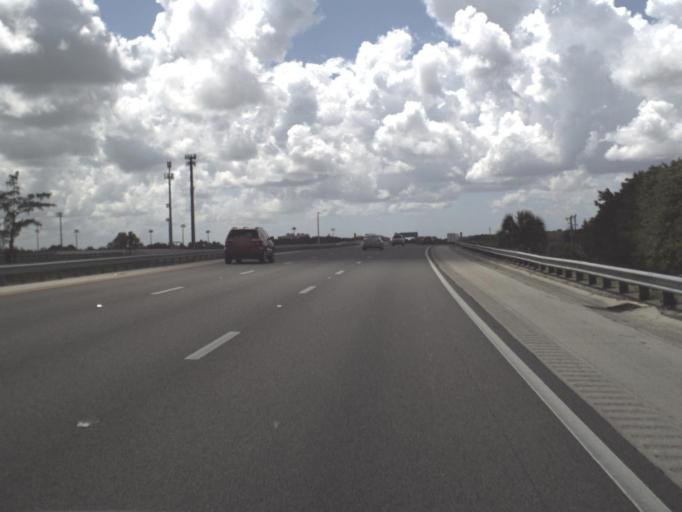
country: US
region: Florida
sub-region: Collier County
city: Vineyards
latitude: 26.2458
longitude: -81.7378
